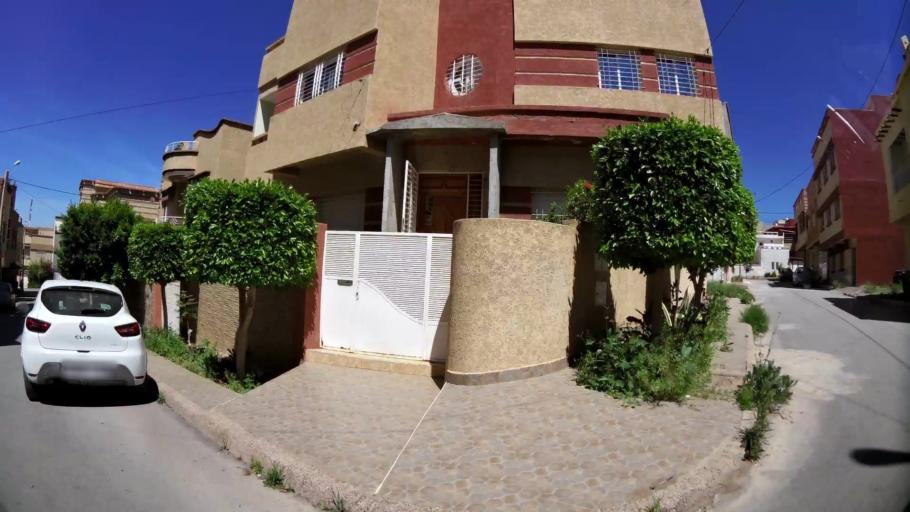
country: MA
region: Oriental
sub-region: Oujda-Angad
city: Oujda
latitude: 34.6474
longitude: -1.9090
